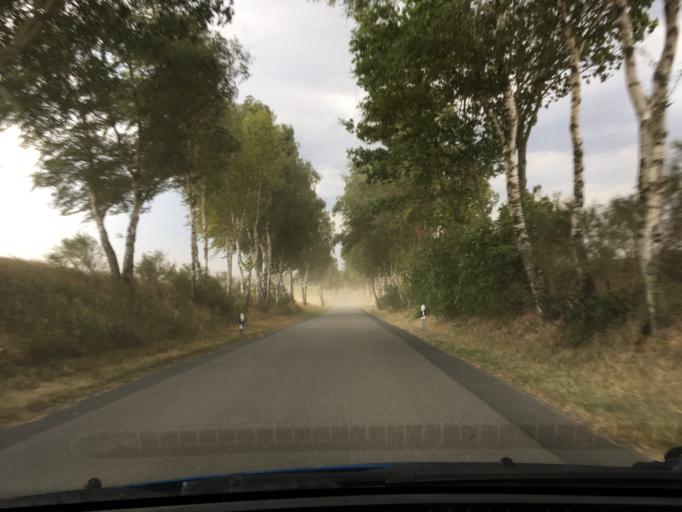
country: DE
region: Lower Saxony
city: Hanstedt Eins
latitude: 53.0662
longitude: 10.3836
